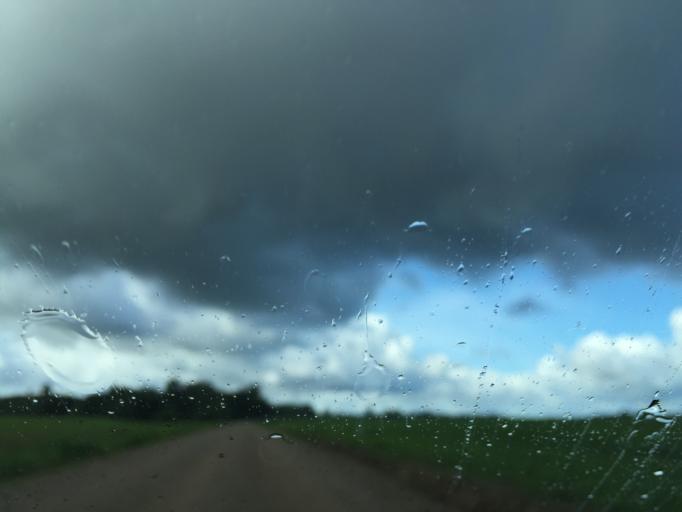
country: LV
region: Talsu Rajons
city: Sabile
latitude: 57.0531
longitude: 22.4619
